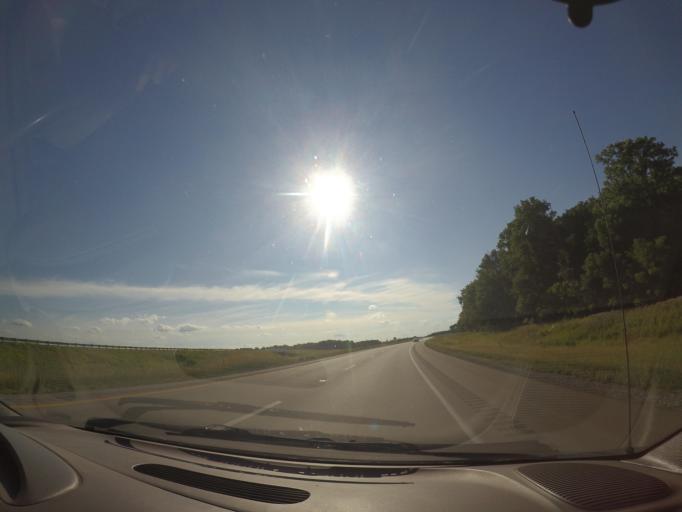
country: US
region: Ohio
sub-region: Henry County
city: Liberty Center
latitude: 41.4158
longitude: -84.0607
